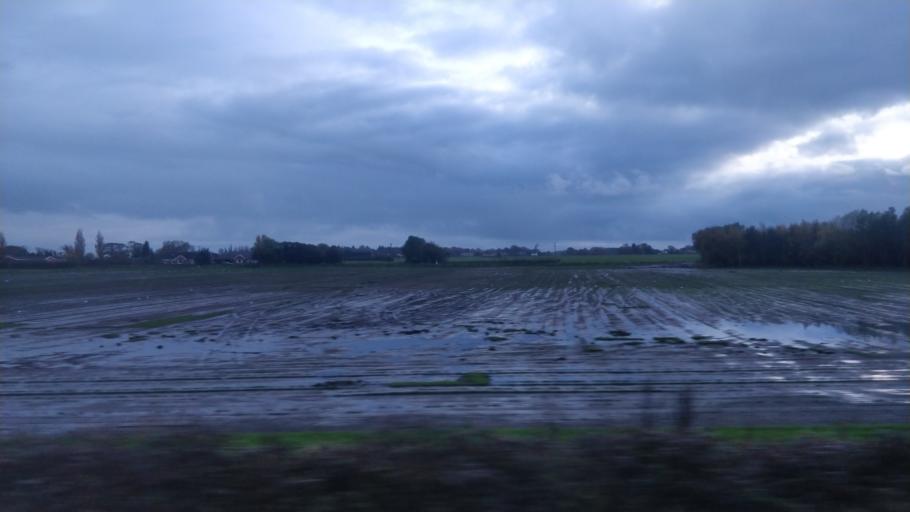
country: GB
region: England
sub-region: Lancashire
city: Ormskirk
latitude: 53.6216
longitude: -2.9055
